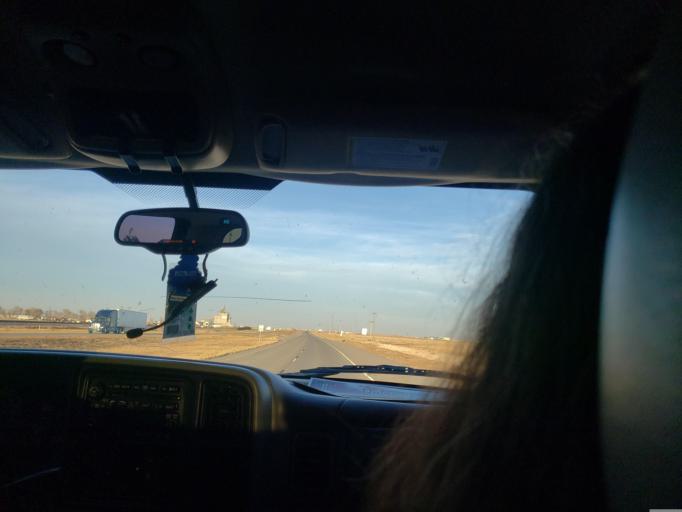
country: US
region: Oklahoma
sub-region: Texas County
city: Guymon
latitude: 36.7630
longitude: -101.3517
